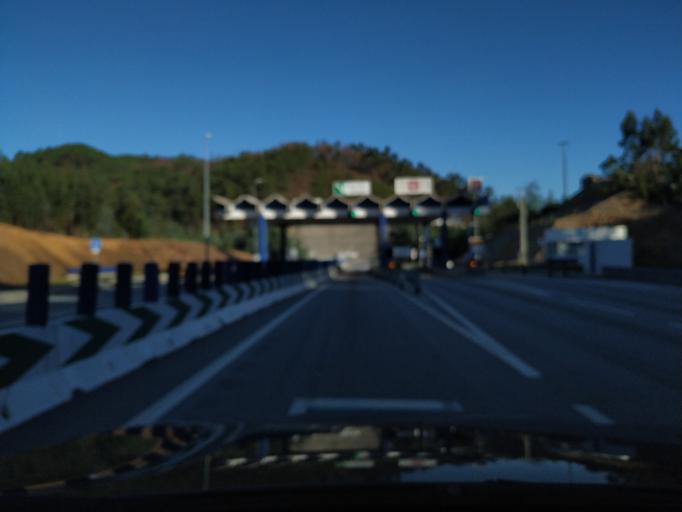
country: PT
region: Aveiro
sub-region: Oliveira de Azemeis
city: Vila Cha
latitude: 40.8764
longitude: -8.4294
